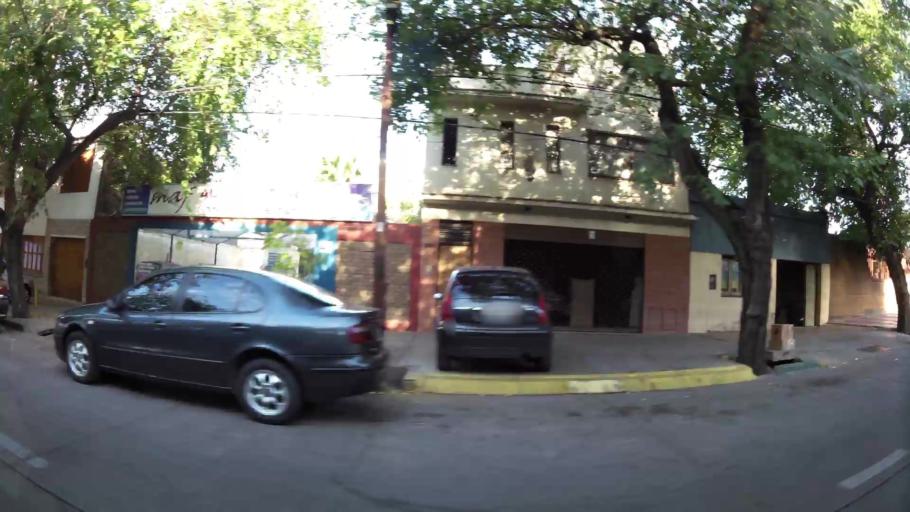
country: AR
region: Mendoza
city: Mendoza
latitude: -32.9034
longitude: -68.8420
